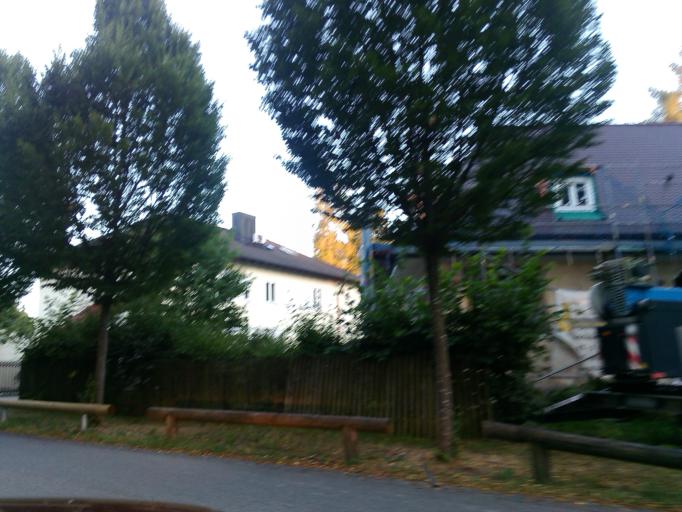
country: DE
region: Bavaria
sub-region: Upper Bavaria
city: Planegg
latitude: 48.1078
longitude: 11.4205
